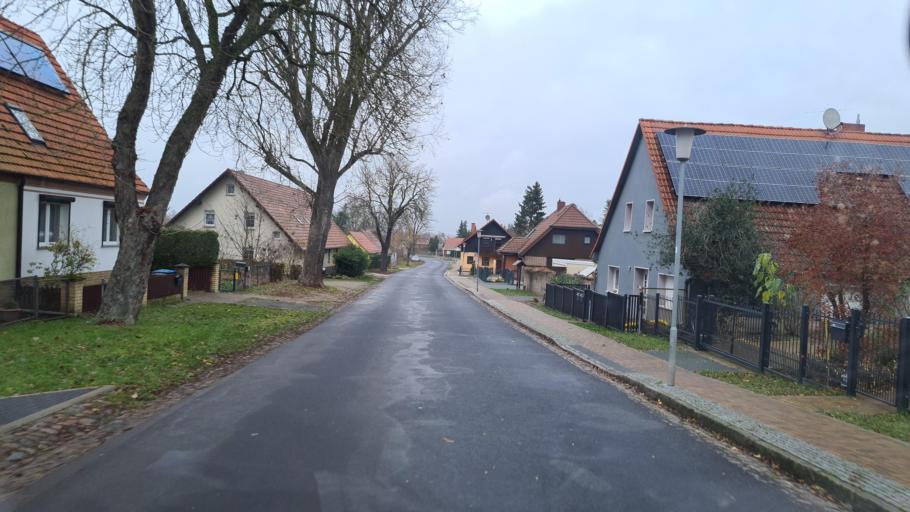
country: DE
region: Brandenburg
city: Nauen
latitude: 52.6224
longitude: 12.7947
